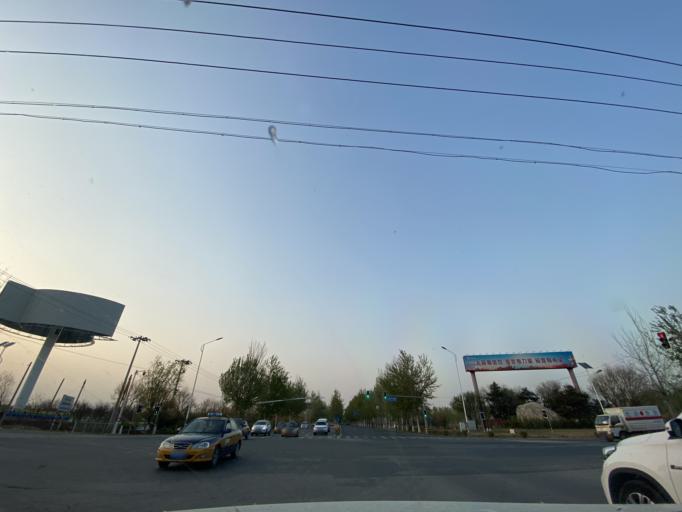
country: CN
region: Beijing
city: Weishanzhuang
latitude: 39.6153
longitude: 116.4095
